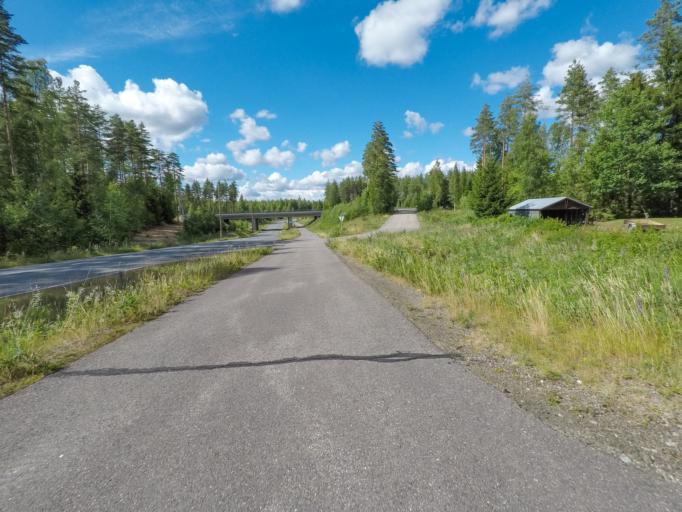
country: FI
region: South Karelia
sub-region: Lappeenranta
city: Joutseno
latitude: 61.0908
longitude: 28.3540
